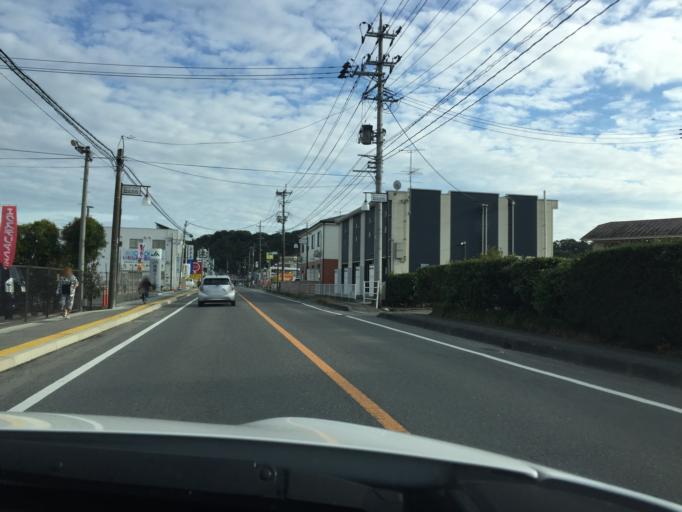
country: JP
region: Fukushima
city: Iwaki
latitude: 37.0607
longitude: 140.8588
